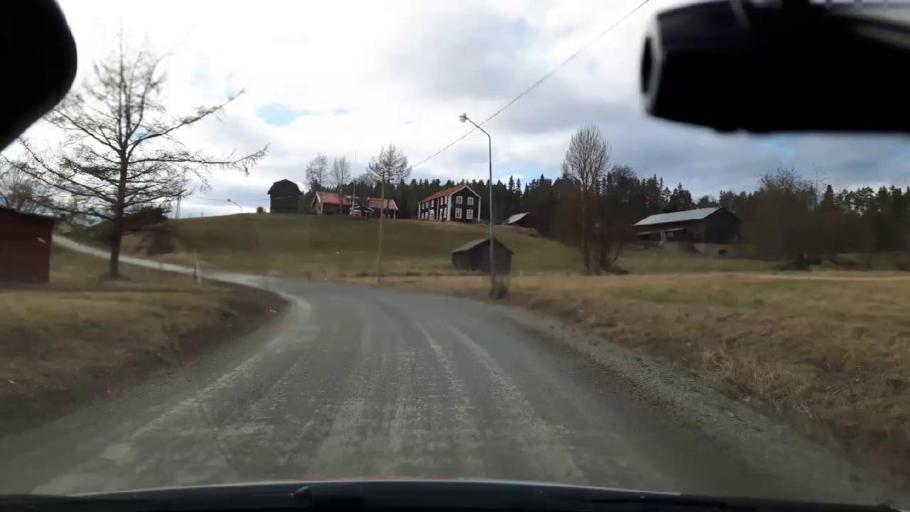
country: SE
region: Jaemtland
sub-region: OEstersunds Kommun
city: Brunflo
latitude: 62.9533
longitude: 14.6558
